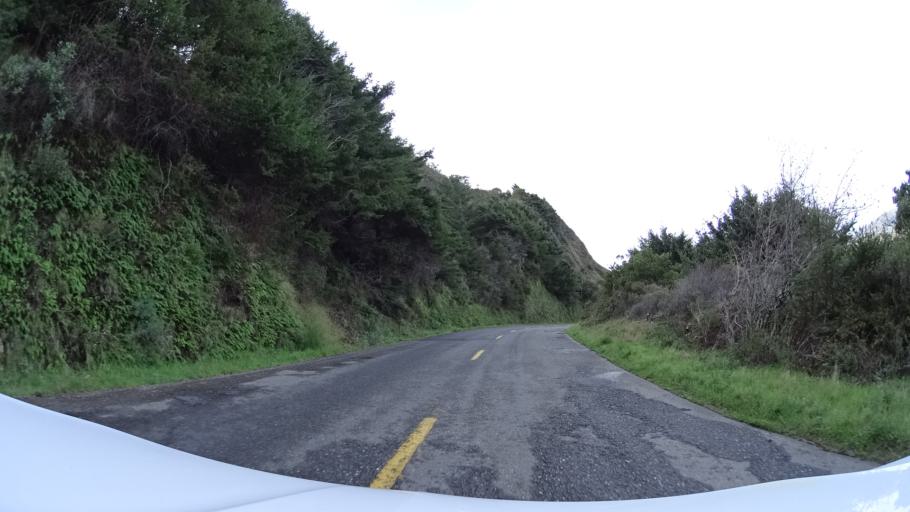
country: US
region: California
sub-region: Humboldt County
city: Ferndale
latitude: 40.3487
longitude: -124.3565
